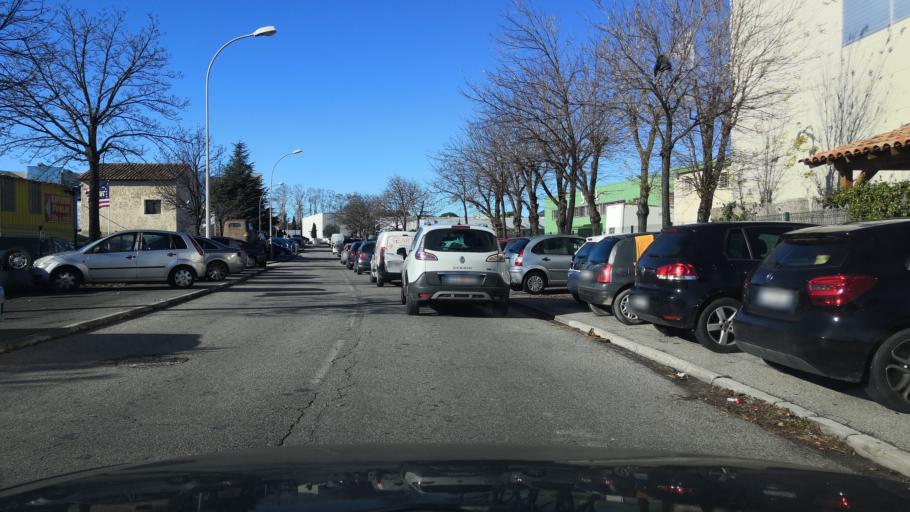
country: FR
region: Provence-Alpes-Cote d'Azur
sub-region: Departement des Bouches-du-Rhone
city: Aubagne
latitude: 43.2848
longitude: 5.5968
